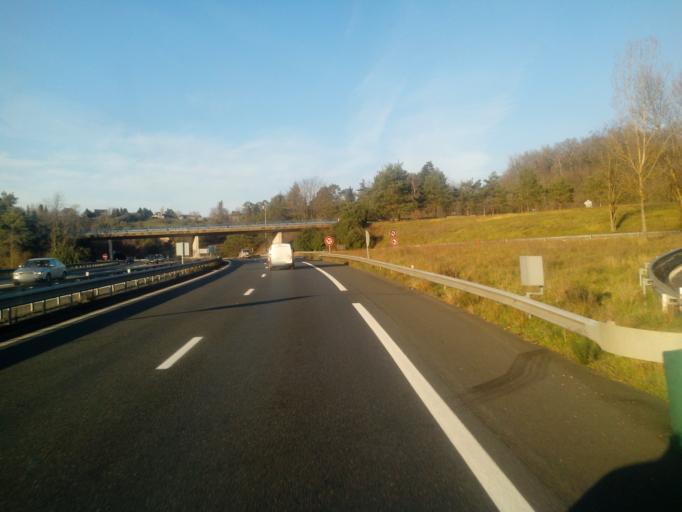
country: FR
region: Limousin
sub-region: Departement de la Correze
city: Brive-la-Gaillarde
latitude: 45.0974
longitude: 1.5202
